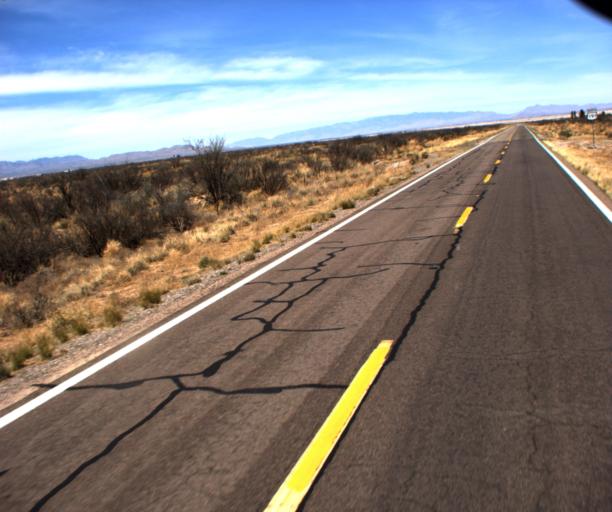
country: US
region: Arizona
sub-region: Cochise County
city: Willcox
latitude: 32.1135
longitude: -109.9125
